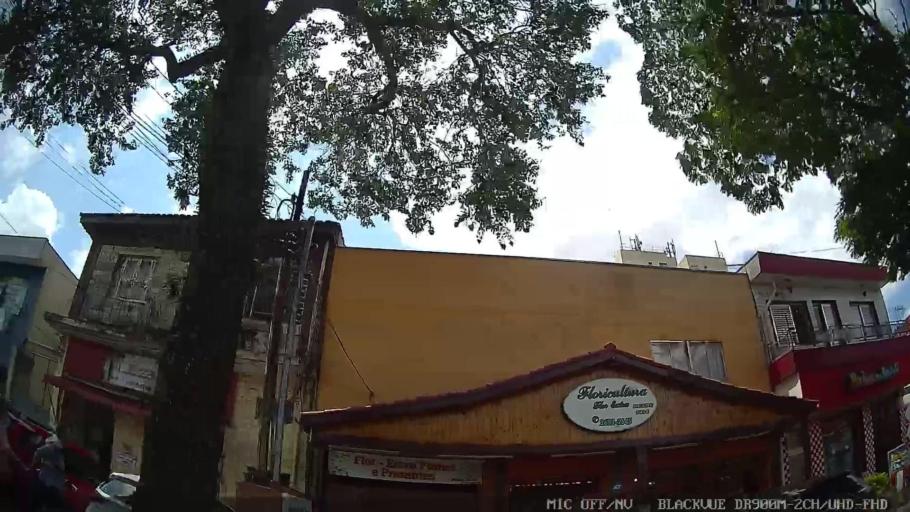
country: BR
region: Sao Paulo
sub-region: Guarulhos
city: Guarulhos
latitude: -23.5242
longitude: -46.5086
